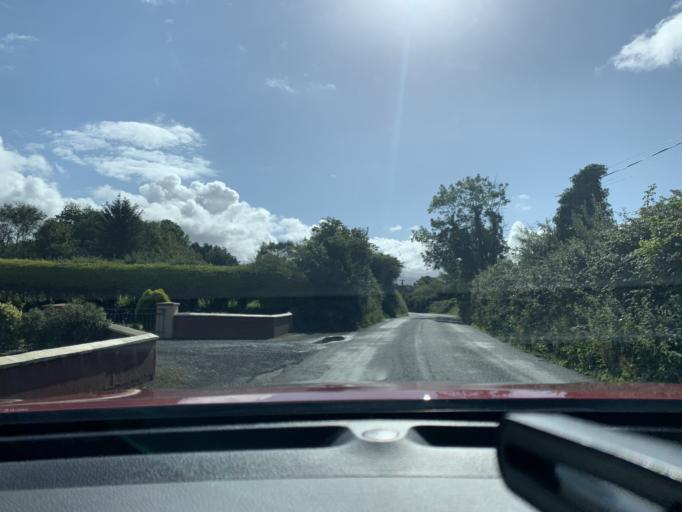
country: IE
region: Connaught
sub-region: Sligo
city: Strandhill
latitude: 54.3390
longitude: -8.5391
